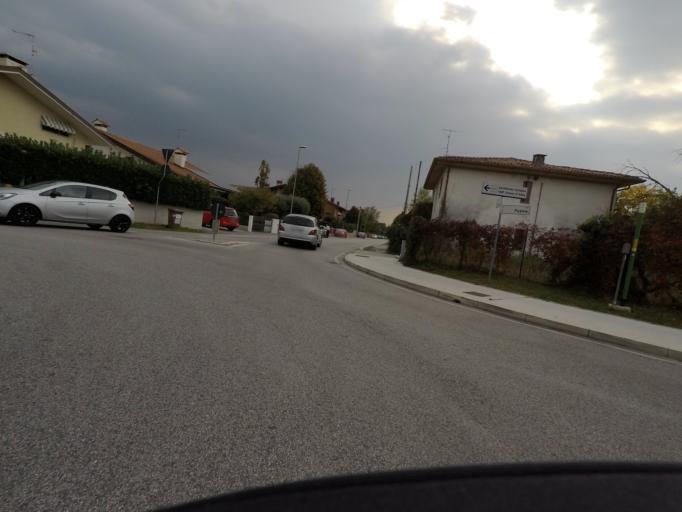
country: IT
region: Friuli Venezia Giulia
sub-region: Provincia di Udine
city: Feletto Umberto
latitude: 46.0933
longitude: 13.2425
